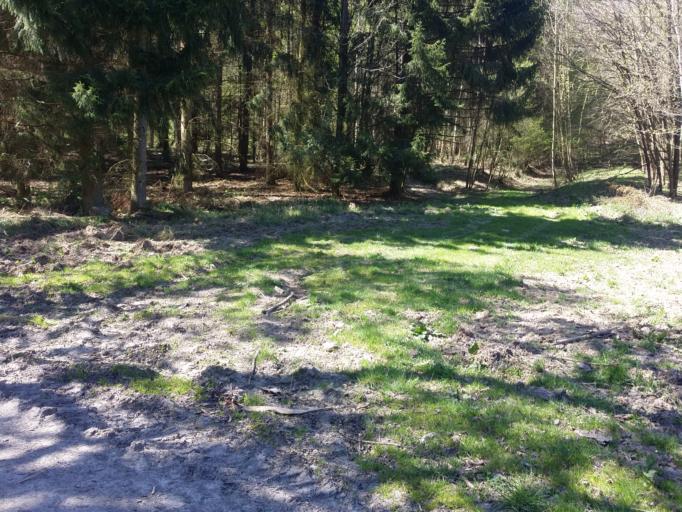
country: DE
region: Saxony-Anhalt
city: Ballenstedt
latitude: 51.6773
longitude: 11.2249
